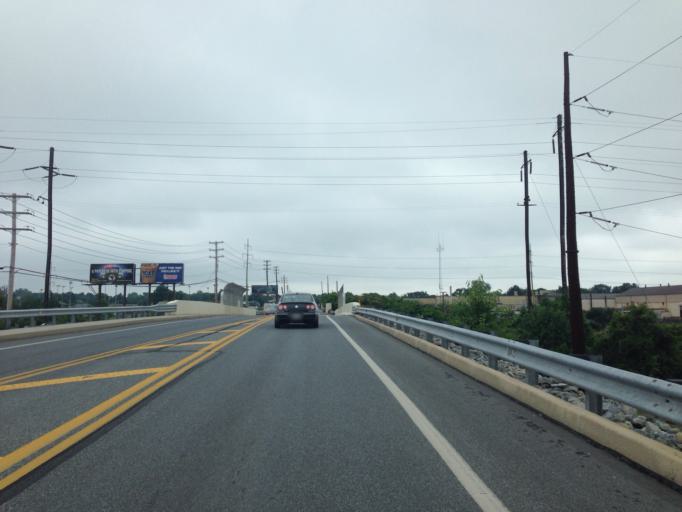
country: US
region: Pennsylvania
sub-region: Lancaster County
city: Lancaster
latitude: 40.0582
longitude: -76.3211
